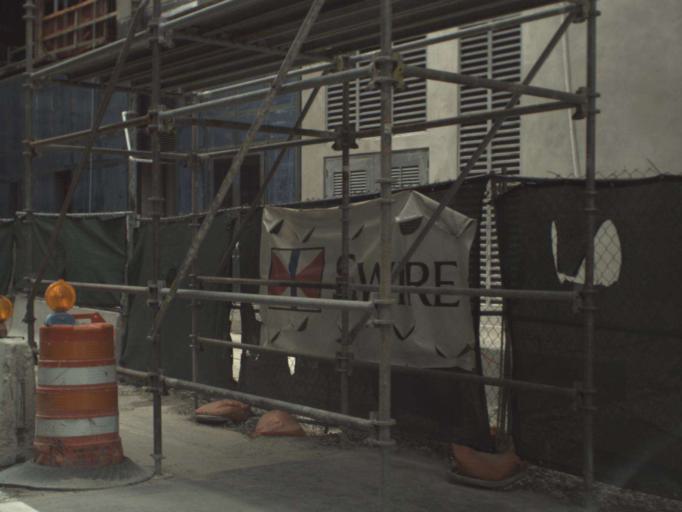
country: US
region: Florida
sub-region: Miami-Dade County
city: Miami
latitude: 25.7674
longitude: -80.1924
